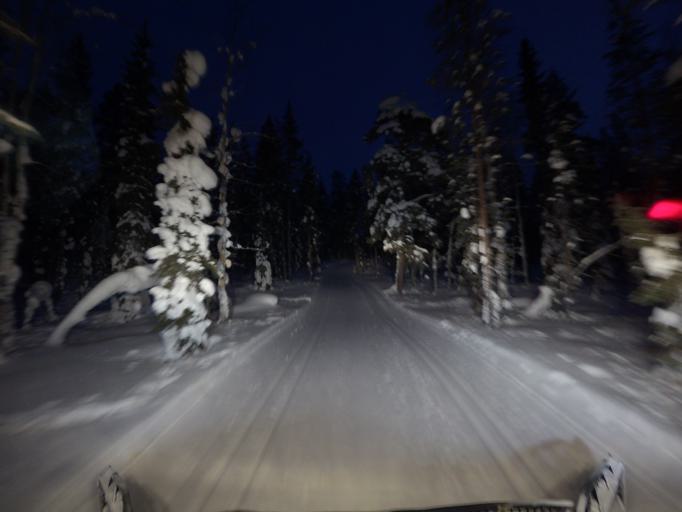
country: FI
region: Lapland
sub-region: Tunturi-Lappi
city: Kolari
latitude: 67.5966
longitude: 24.1102
